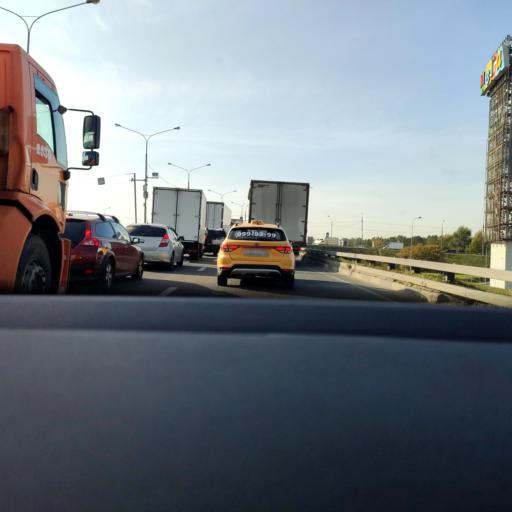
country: RU
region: Moskovskaya
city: Kotel'niki
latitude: 55.6570
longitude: 37.8441
